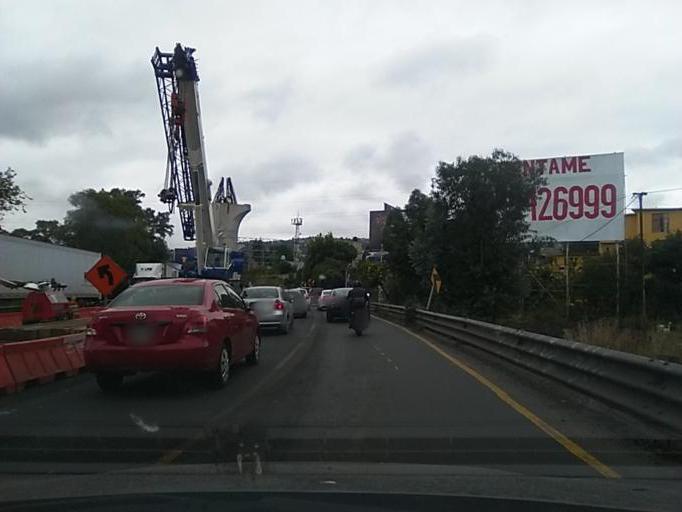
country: MX
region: Mexico City
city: Tlalpan
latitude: 19.2626
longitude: -99.1662
